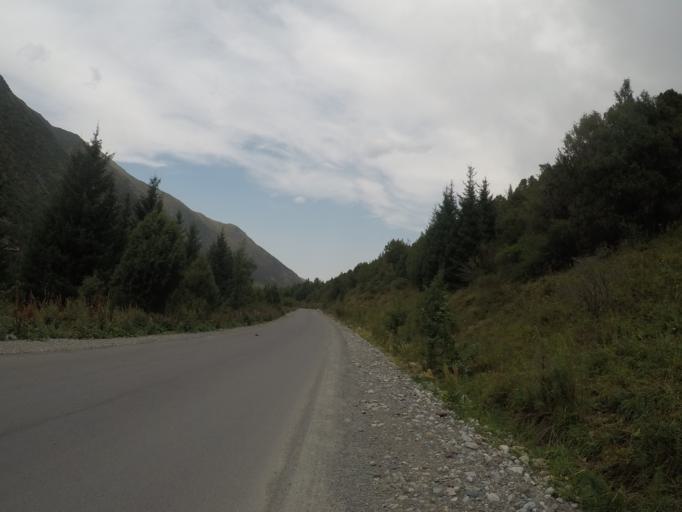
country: KG
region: Chuy
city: Bishkek
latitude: 42.5865
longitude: 74.4840
